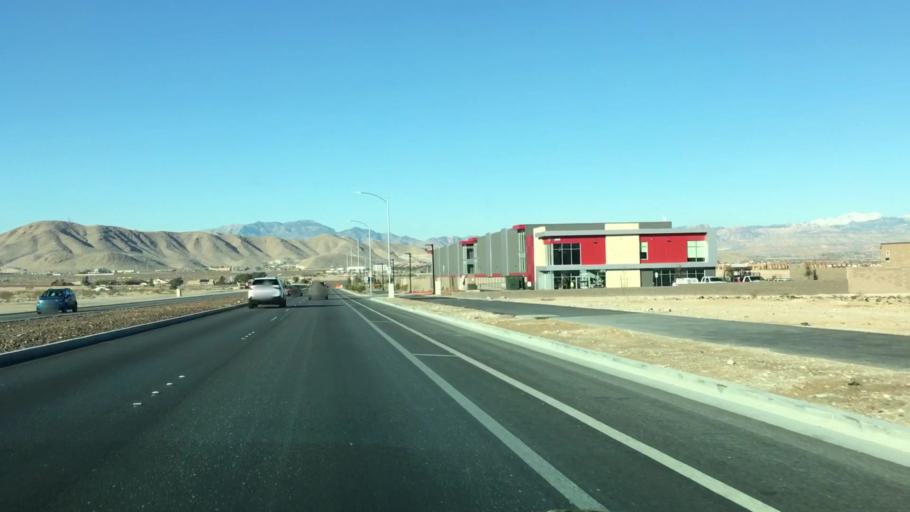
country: US
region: Nevada
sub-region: Clark County
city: Enterprise
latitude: 35.9600
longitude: -115.1428
